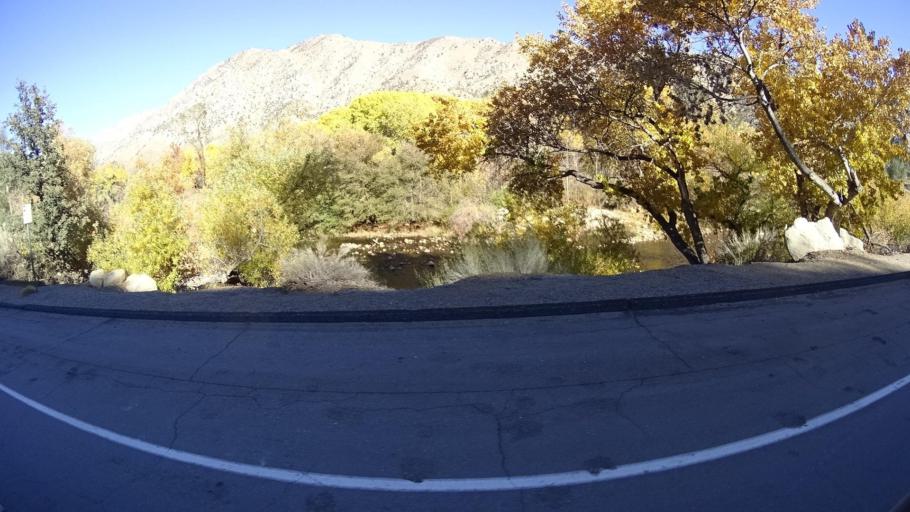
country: US
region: California
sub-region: Kern County
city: Kernville
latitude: 35.7515
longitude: -118.4241
